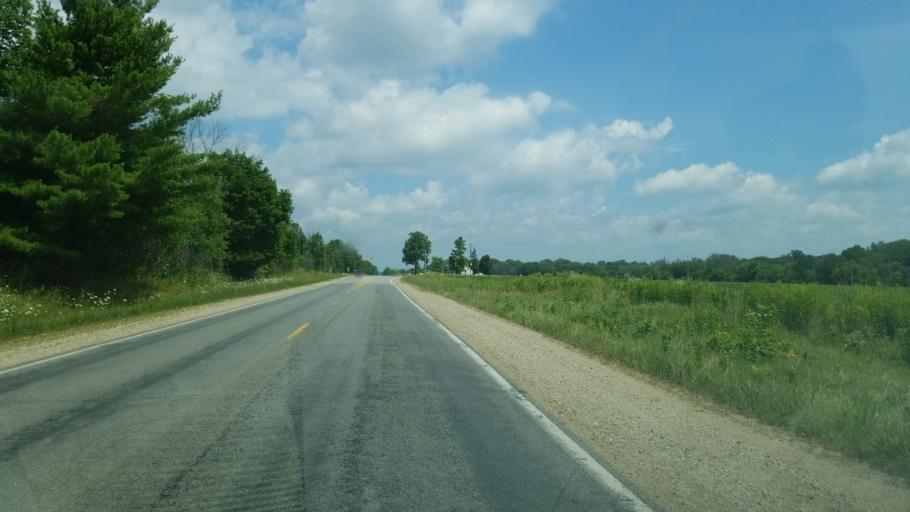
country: US
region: Michigan
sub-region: Montcalm County
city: Howard City
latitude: 43.3644
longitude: -85.4790
